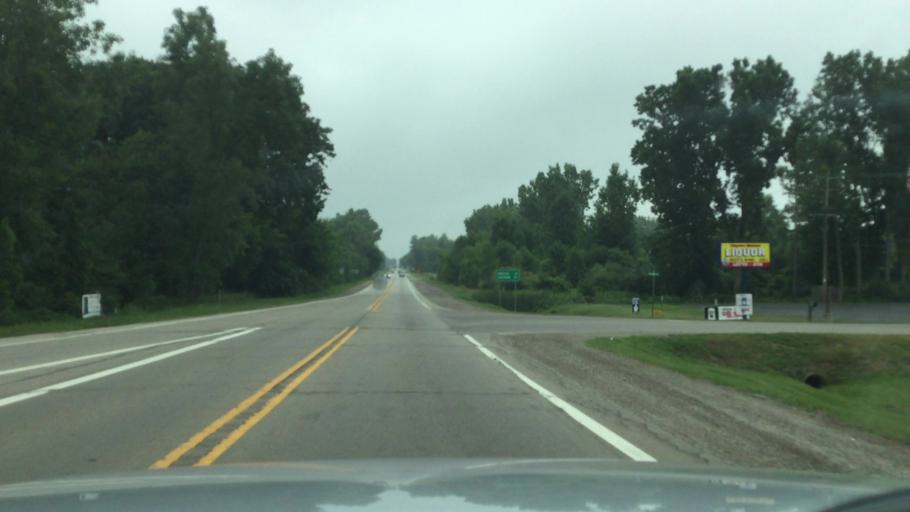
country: US
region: Michigan
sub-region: Shiawassee County
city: Durand
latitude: 42.9666
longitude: -83.9288
